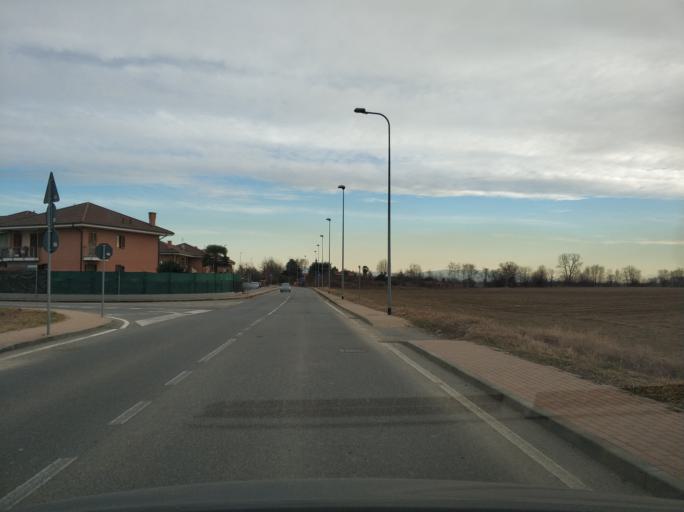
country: IT
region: Piedmont
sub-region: Provincia di Torino
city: San Maurizio
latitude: 45.2070
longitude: 7.6327
